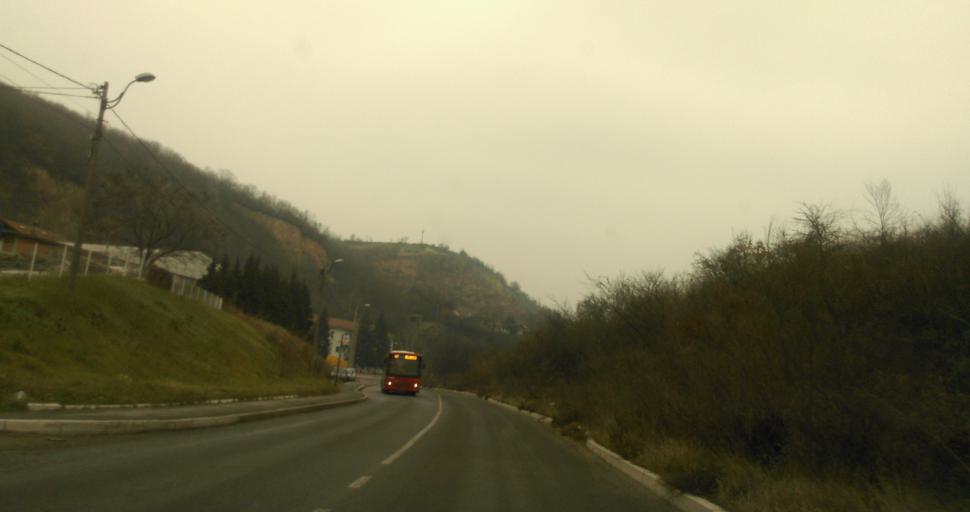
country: RS
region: Central Serbia
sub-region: Belgrade
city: Rakovica
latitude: 44.7276
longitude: 20.4480
